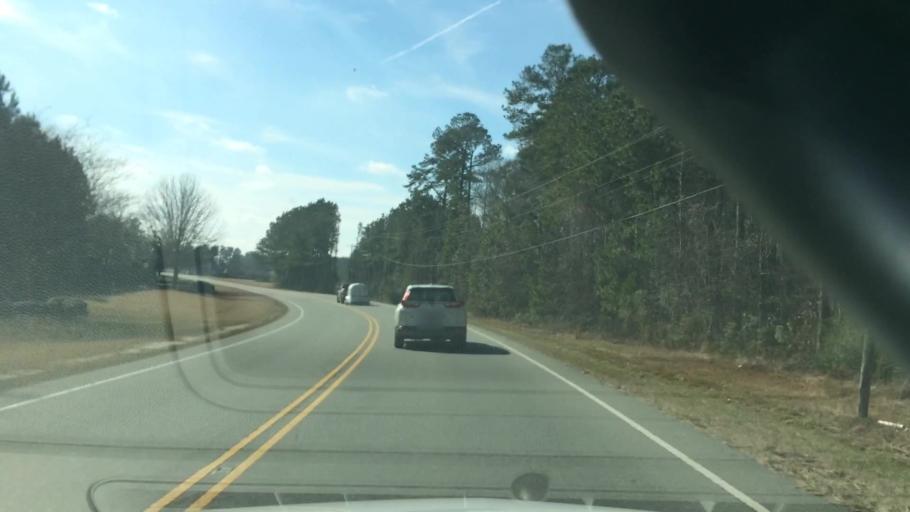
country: US
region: North Carolina
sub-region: Duplin County
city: Wallace
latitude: 34.7630
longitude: -77.9439
